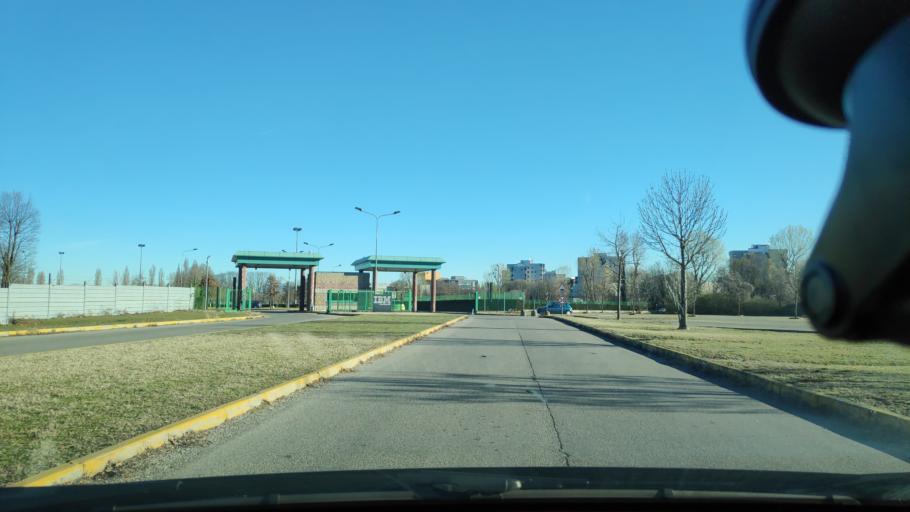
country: IT
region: Lombardy
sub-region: Citta metropolitana di Milano
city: San Bovio-San Felice
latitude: 45.4697
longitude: 9.3023
